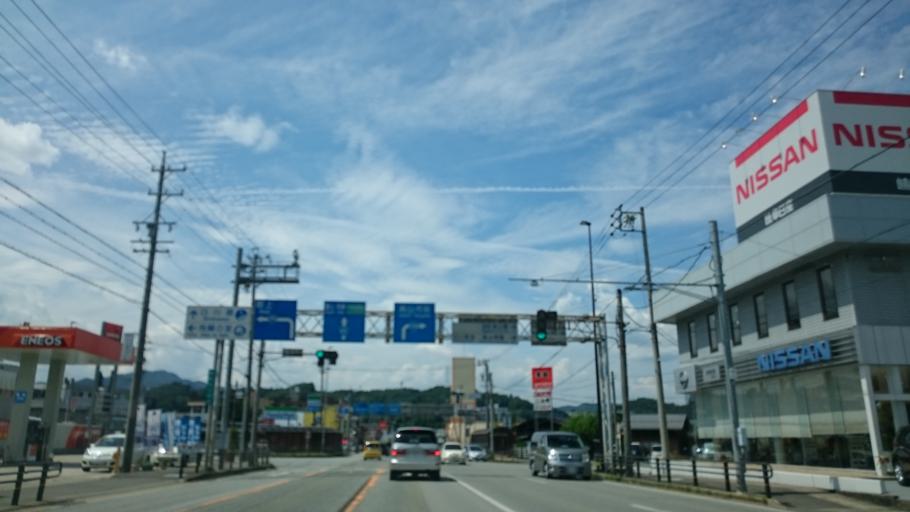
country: JP
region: Gifu
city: Takayama
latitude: 36.1375
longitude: 137.2450
